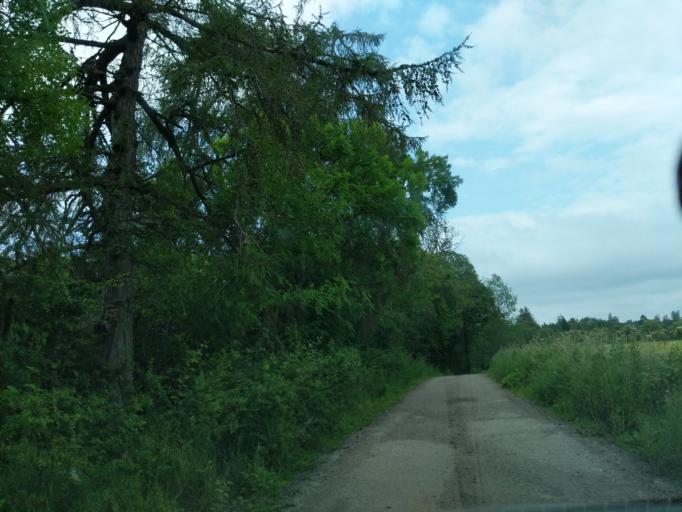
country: GB
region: Scotland
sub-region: Moray
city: Rothes
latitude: 57.4745
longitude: -3.2376
